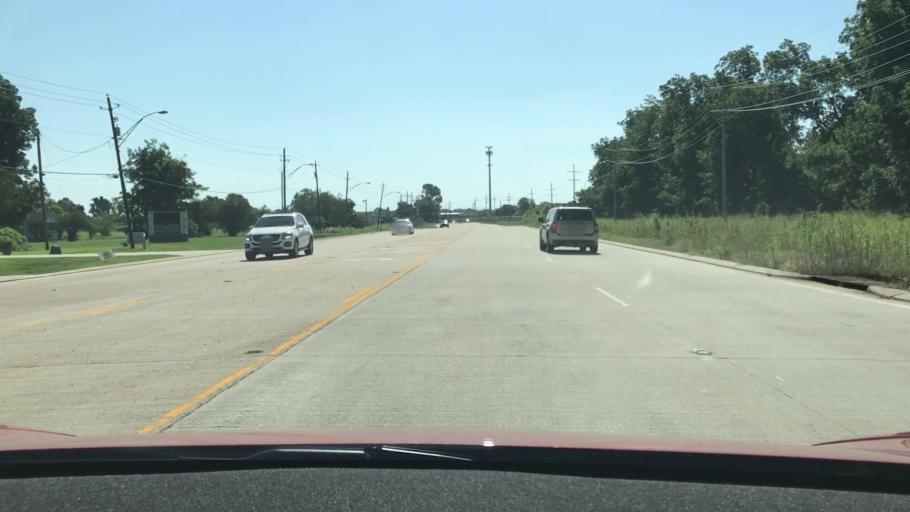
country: US
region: Louisiana
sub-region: Bossier Parish
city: Bossier City
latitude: 32.4008
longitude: -93.6986
